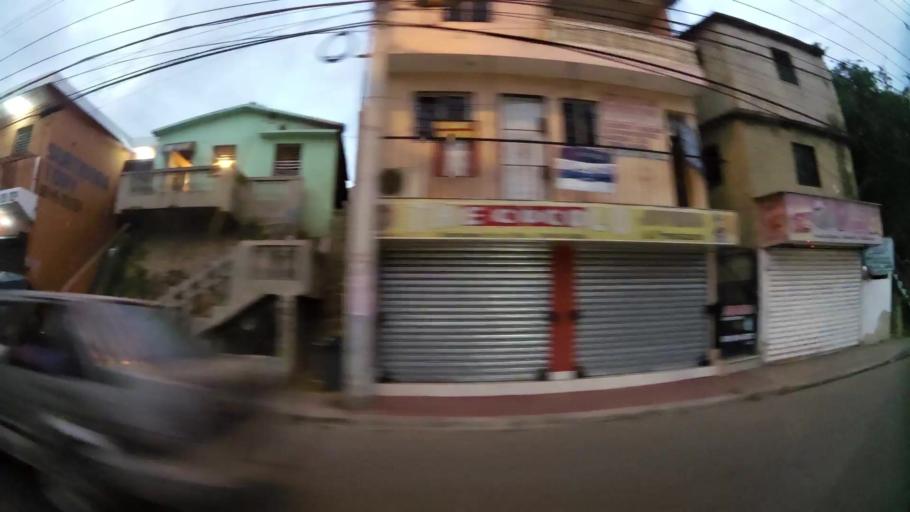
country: DO
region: Santo Domingo
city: Santo Domingo Oeste
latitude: 18.5247
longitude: -70.0235
